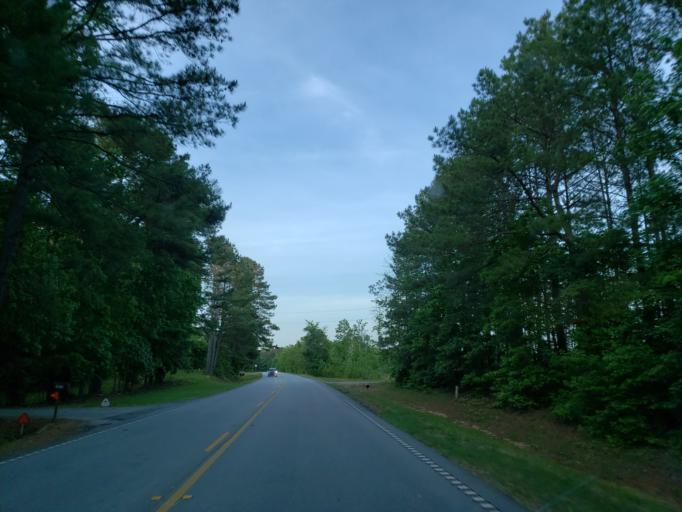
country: US
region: Georgia
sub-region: Fulton County
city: Chattahoochee Hills
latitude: 33.5212
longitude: -84.8732
